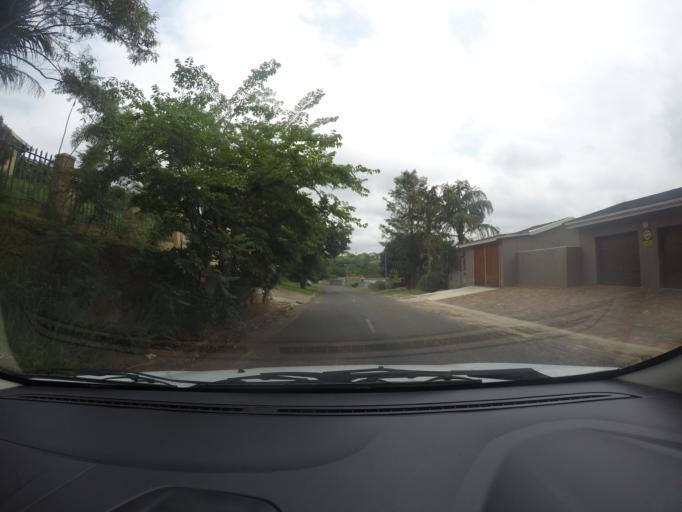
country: ZA
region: KwaZulu-Natal
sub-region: uThungulu District Municipality
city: Empangeni
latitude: -28.7502
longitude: 31.8895
